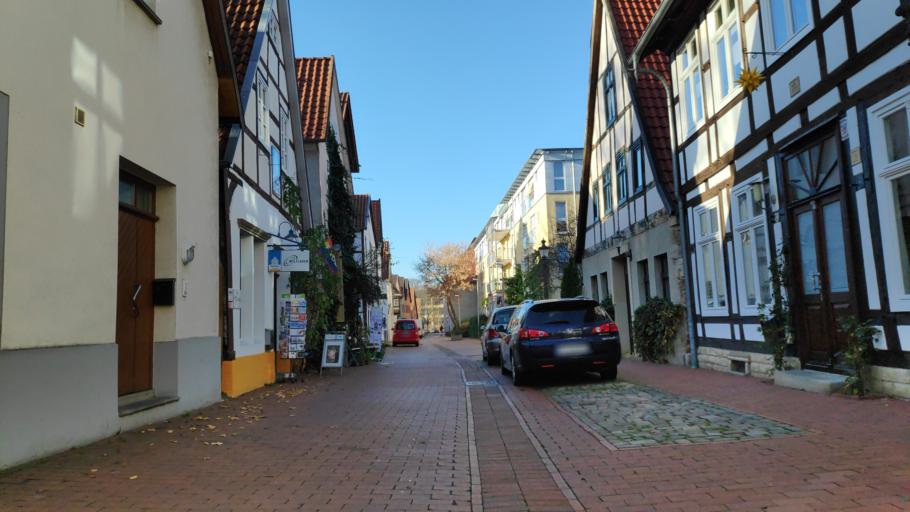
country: DE
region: North Rhine-Westphalia
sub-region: Regierungsbezirk Detmold
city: Minden
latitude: 52.2885
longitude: 8.9140
